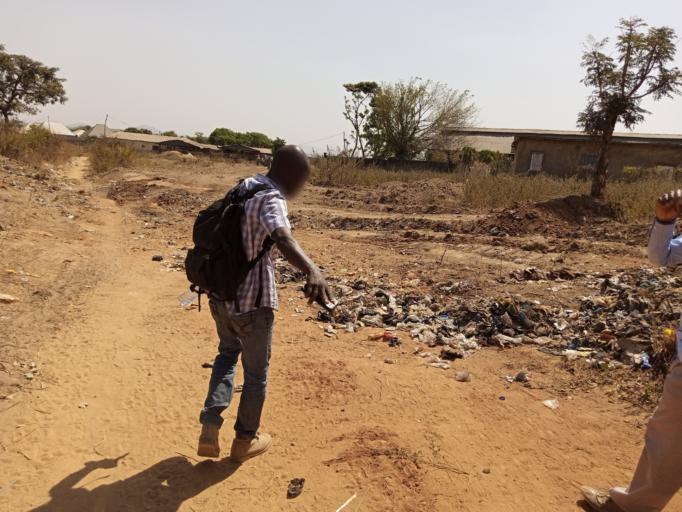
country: NG
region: Abuja Federal Capital Territory
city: Kuje
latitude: 8.9032
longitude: 7.3394
